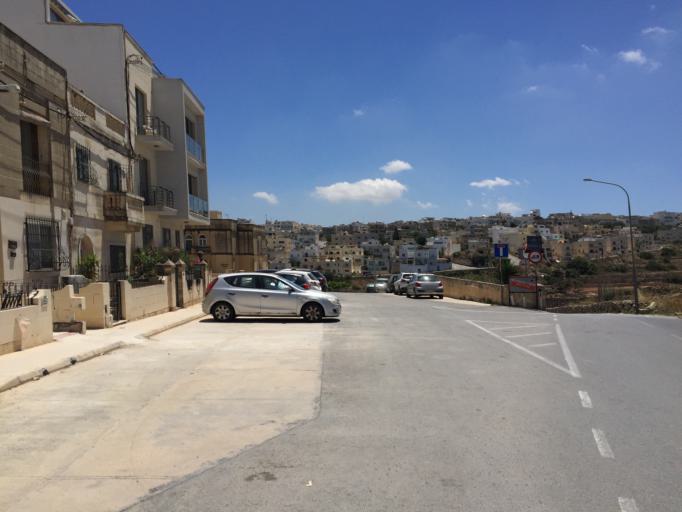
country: MT
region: Is-Swieqi
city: Swieqi
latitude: 35.9189
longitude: 14.4803
